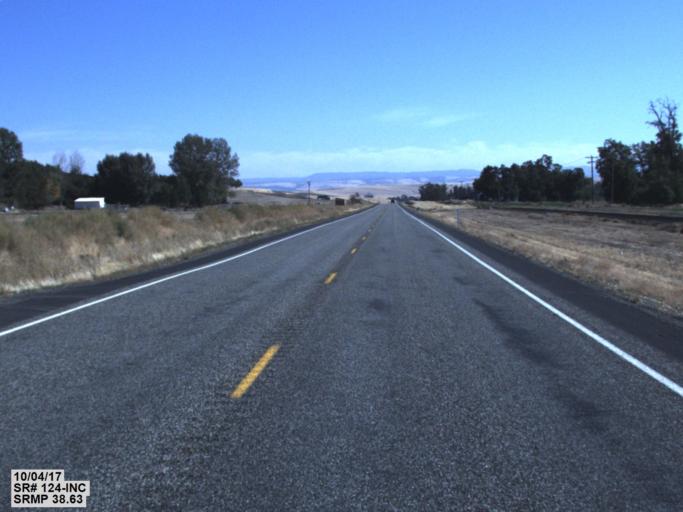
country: US
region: Washington
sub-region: Walla Walla County
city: Waitsburg
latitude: 46.2928
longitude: -118.2648
